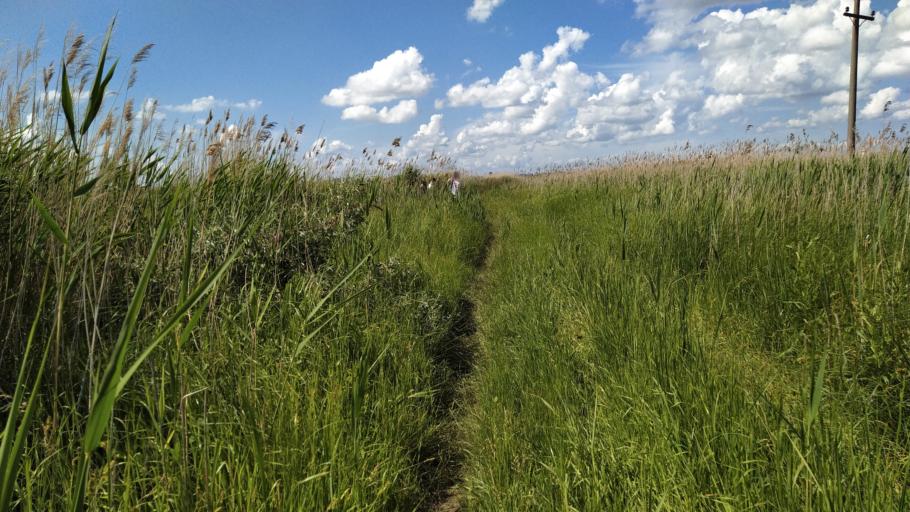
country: RU
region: Rostov
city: Bataysk
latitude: 47.1371
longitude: 39.6696
